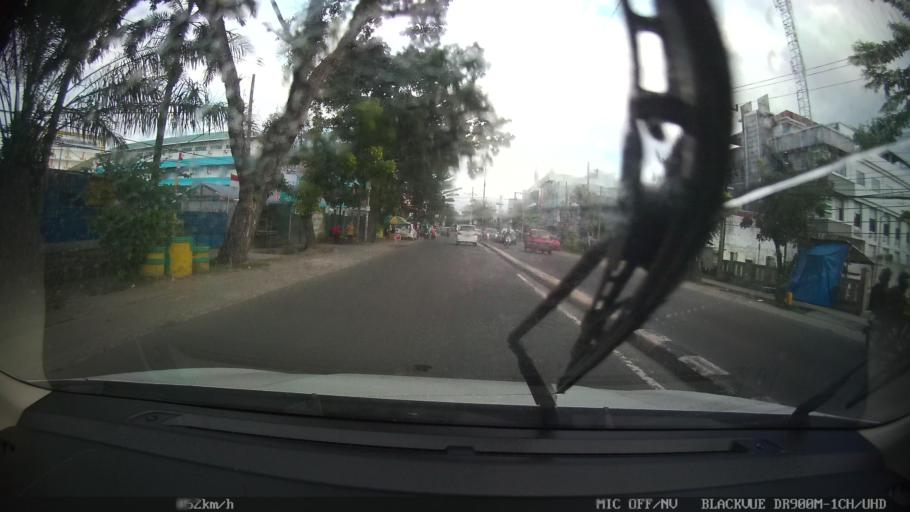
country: ID
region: North Sumatra
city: Medan
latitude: 3.6151
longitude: 98.6722
